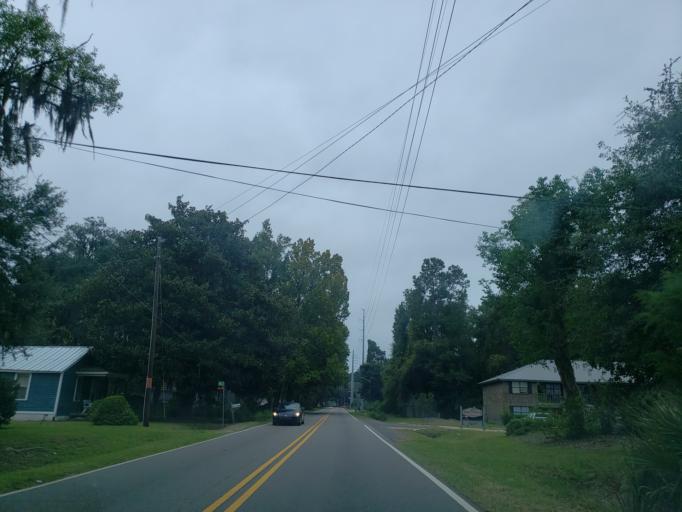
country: US
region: Georgia
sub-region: Chatham County
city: Isle of Hope
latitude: 31.9928
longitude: -81.0778
